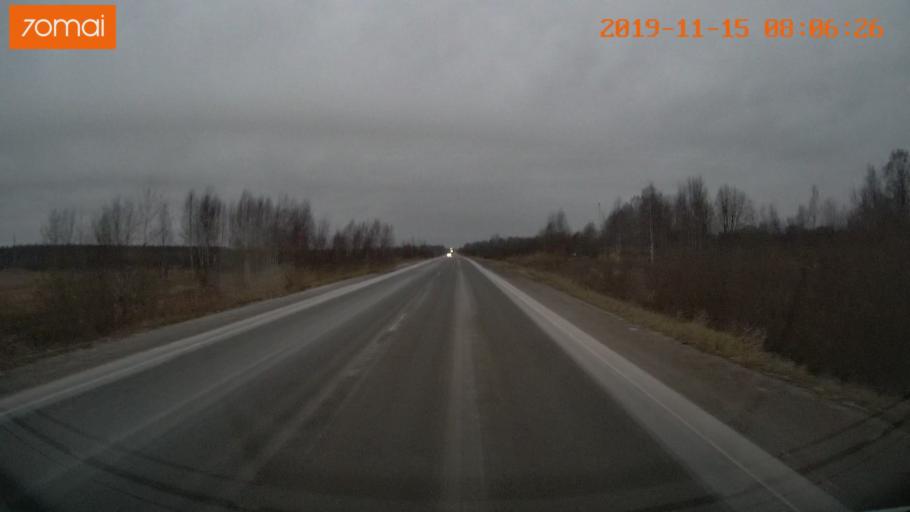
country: RU
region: Vologda
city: Cherepovets
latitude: 59.0211
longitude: 38.0429
